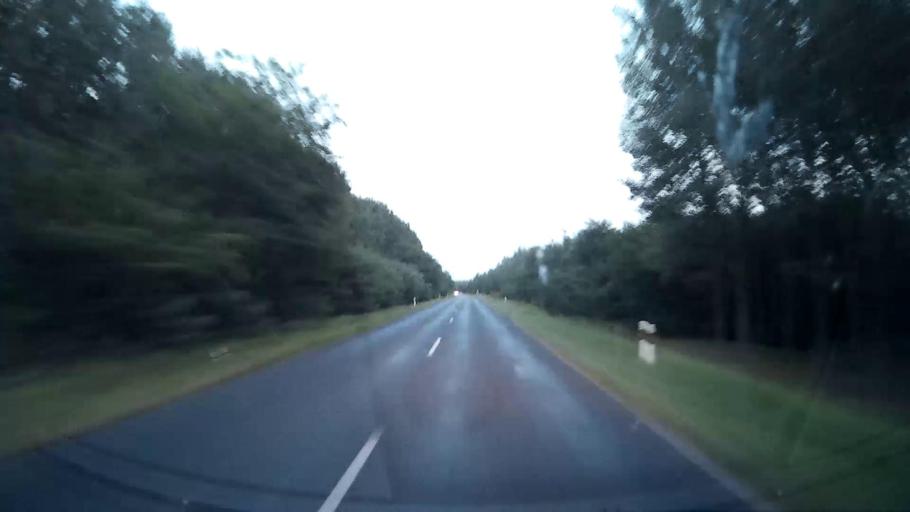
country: HU
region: Pest
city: Cegledbercel
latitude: 47.1988
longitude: 19.7091
